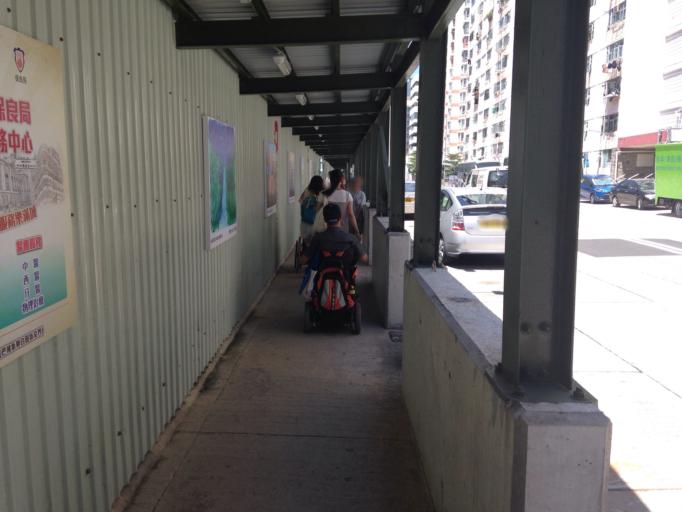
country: HK
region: Sham Shui Po
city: Sham Shui Po
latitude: 22.3335
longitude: 114.1640
